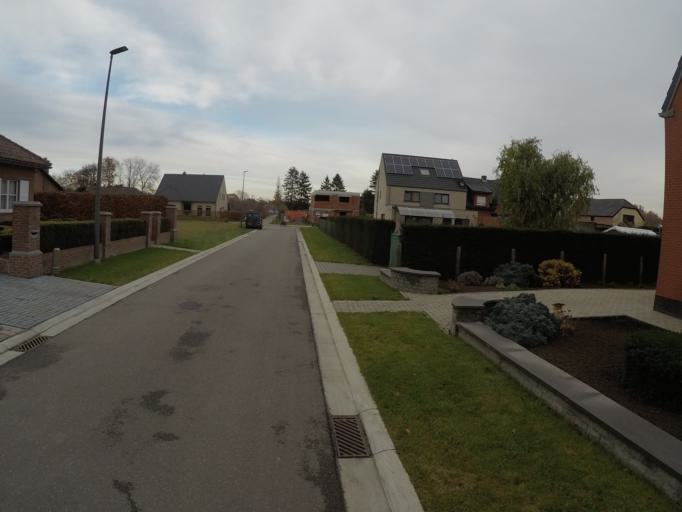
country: BE
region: Flanders
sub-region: Provincie Antwerpen
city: Hulshout
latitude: 51.0775
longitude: 4.7935
